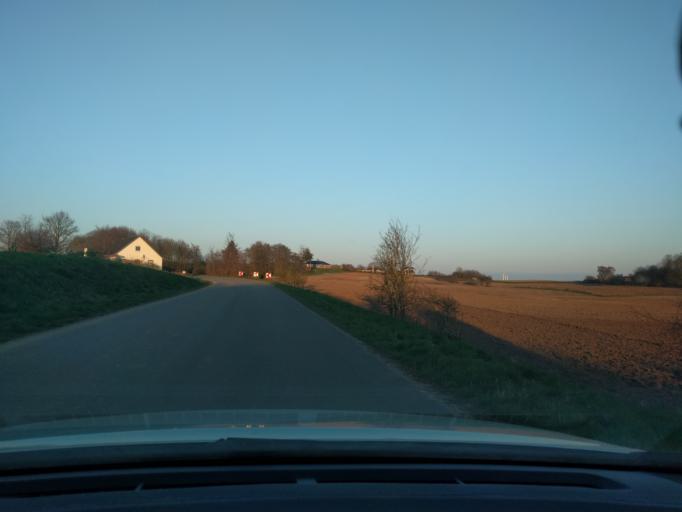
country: DK
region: South Denmark
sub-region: Assens Kommune
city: Glamsbjerg
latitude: 55.2625
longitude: 10.0142
